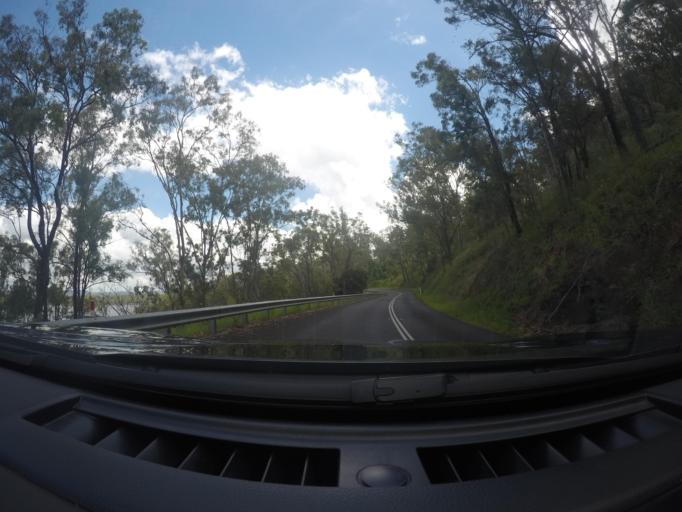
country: AU
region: Queensland
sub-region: Moreton Bay
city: Woodford
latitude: -27.0978
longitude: 152.5628
